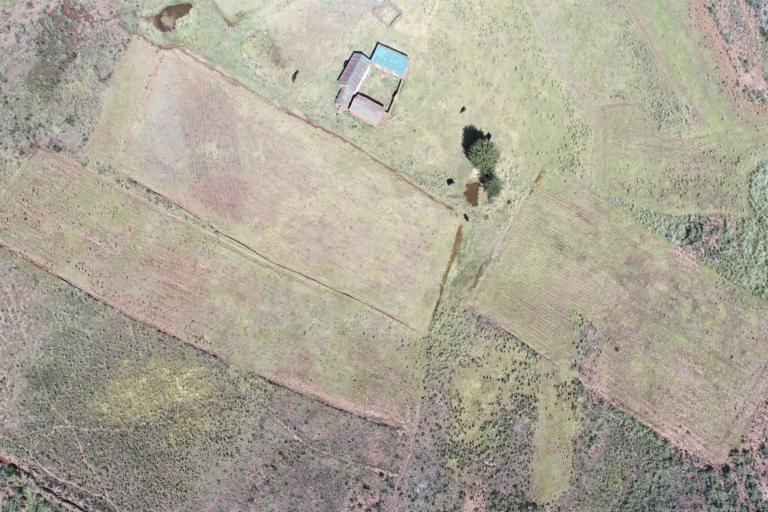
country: BO
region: La Paz
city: Tiahuanaco
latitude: -16.5997
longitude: -68.7575
